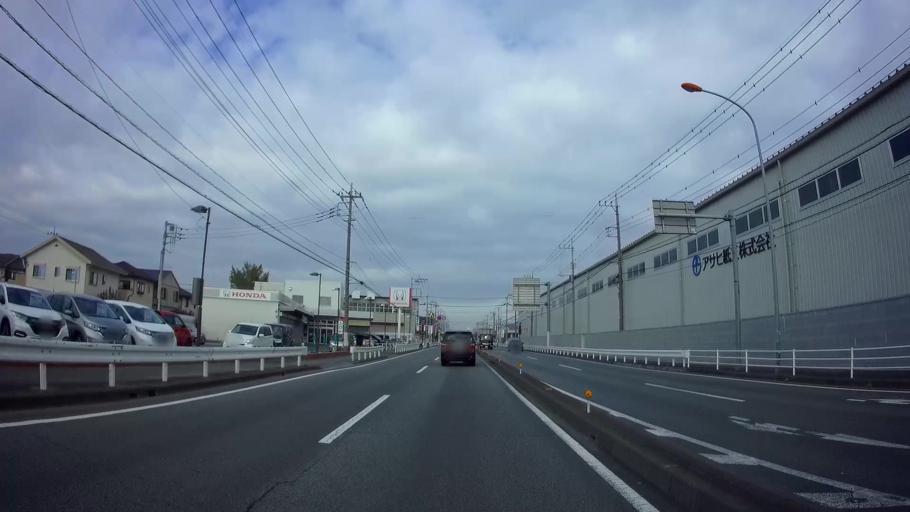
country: JP
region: Saitama
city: Konosu
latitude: 36.0710
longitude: 139.5007
